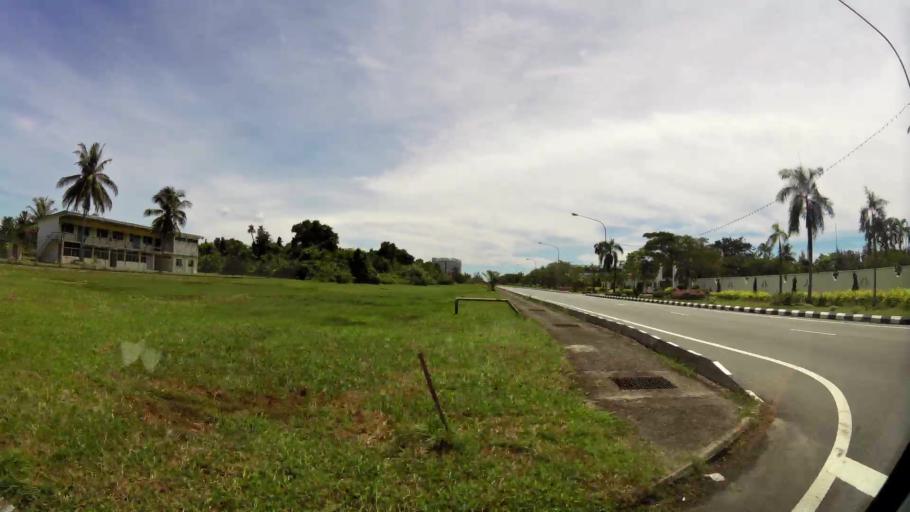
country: BN
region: Belait
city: Kuala Belait
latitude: 4.5960
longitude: 114.2523
